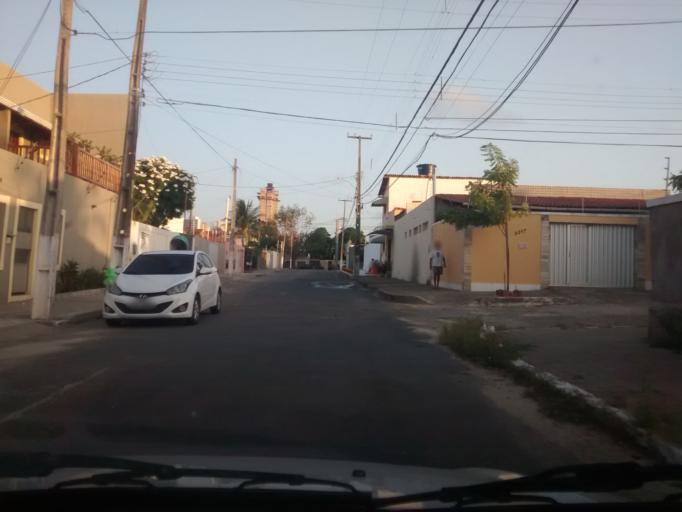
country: BR
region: Rio Grande do Norte
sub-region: Natal
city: Natal
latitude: -5.8731
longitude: -35.1858
